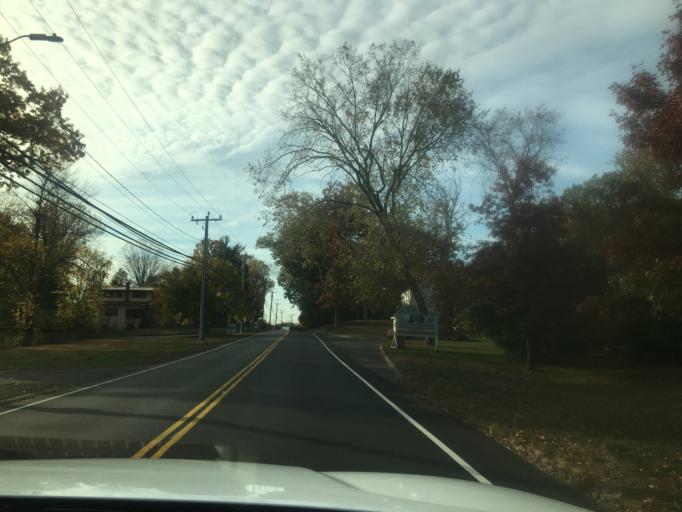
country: US
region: Connecticut
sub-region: Hartford County
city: South Windsor
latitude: 41.8177
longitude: -72.6034
